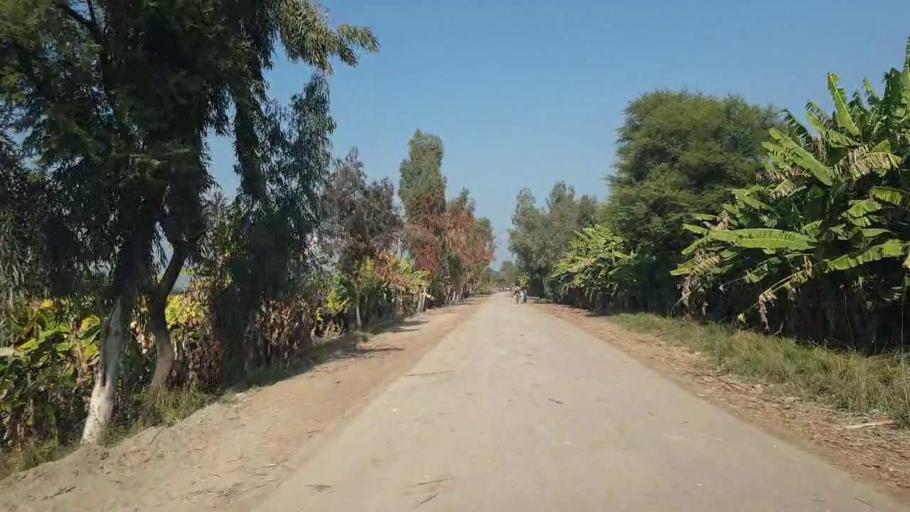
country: PK
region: Sindh
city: Shahdadpur
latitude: 25.9714
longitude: 68.5382
